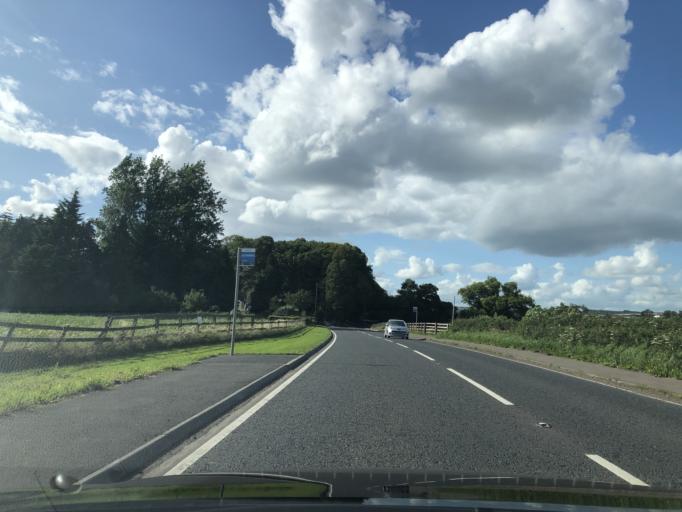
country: GB
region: Northern Ireland
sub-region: Ards District
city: Comber
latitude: 54.5620
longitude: -5.7637
